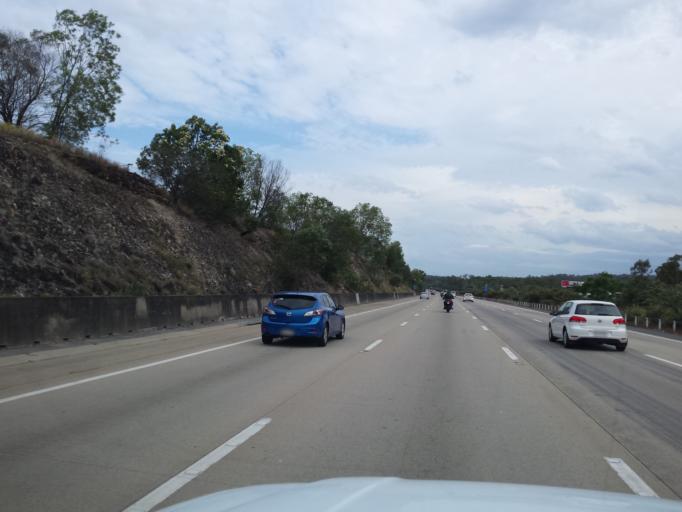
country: AU
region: Queensland
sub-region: Gold Coast
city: Upper Coomera
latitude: -27.9368
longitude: 153.3361
